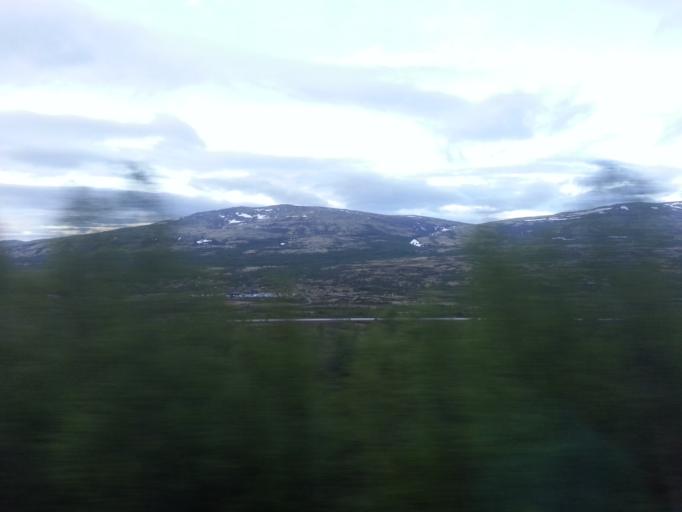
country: NO
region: Oppland
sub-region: Dovre
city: Dovre
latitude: 62.2028
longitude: 9.5316
